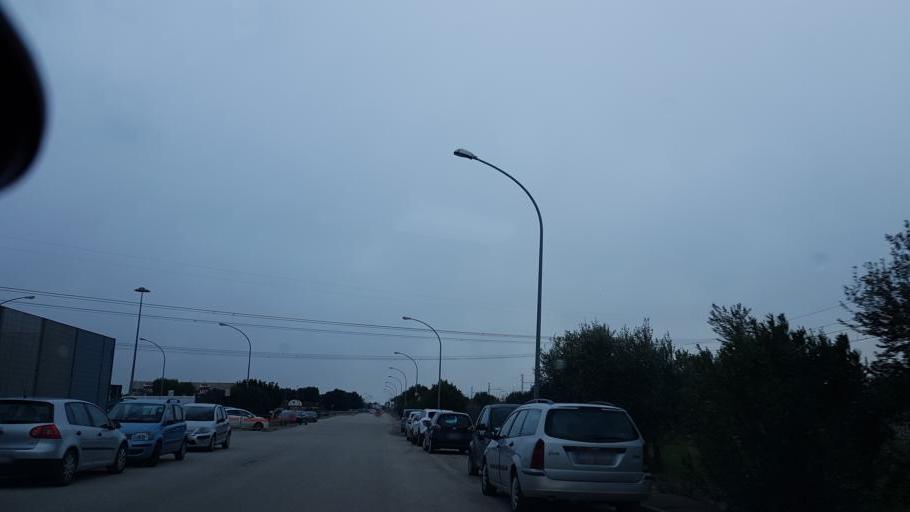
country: IT
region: Apulia
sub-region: Provincia di Brindisi
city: Mesagne
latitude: 40.5813
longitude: 17.8354
